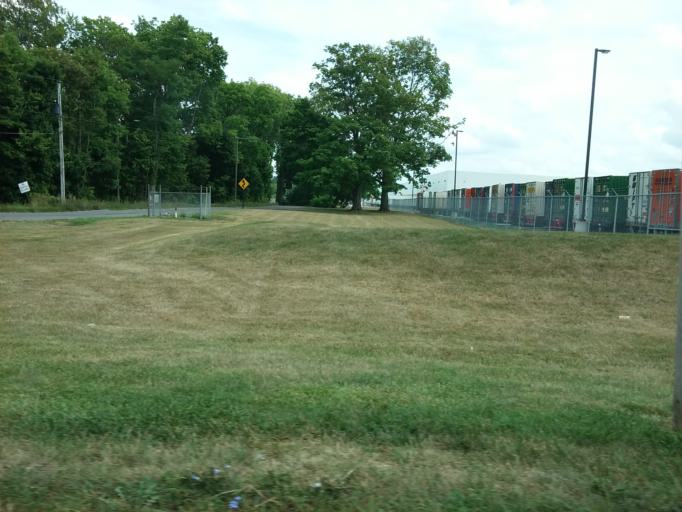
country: US
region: Ohio
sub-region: Hancock County
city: Findlay
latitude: 41.0555
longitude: -83.6885
